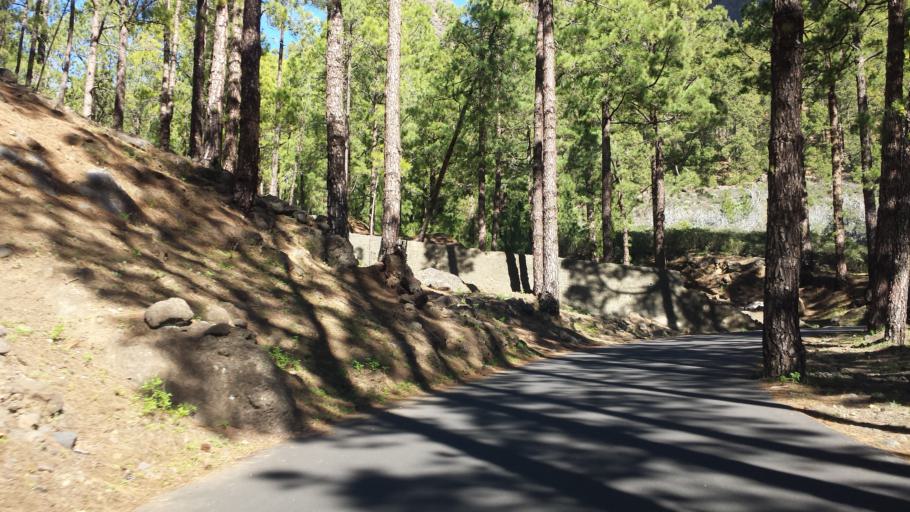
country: ES
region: Canary Islands
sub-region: Provincia de Santa Cruz de Tenerife
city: El Paso
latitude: 28.6946
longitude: -17.8530
